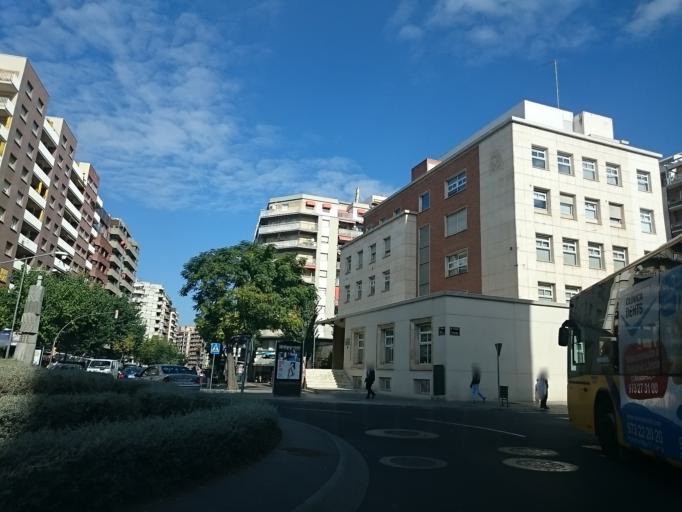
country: ES
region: Catalonia
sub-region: Provincia de Lleida
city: Lleida
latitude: 41.6190
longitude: 0.6194
